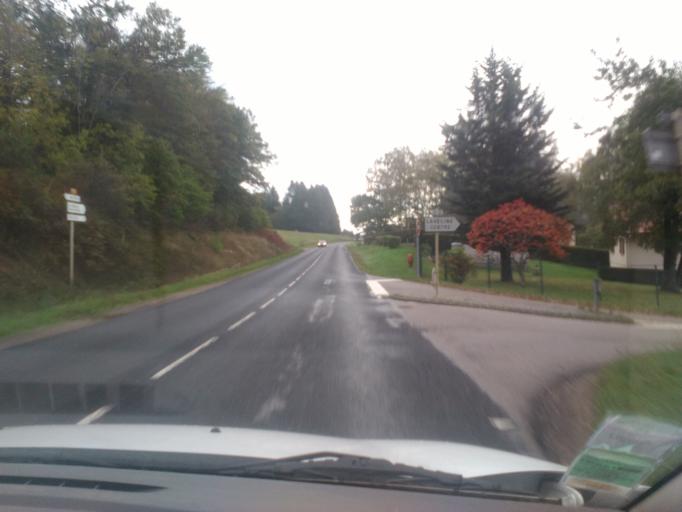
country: FR
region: Lorraine
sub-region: Departement des Vosges
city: Bruyeres
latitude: 48.1884
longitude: 6.7636
